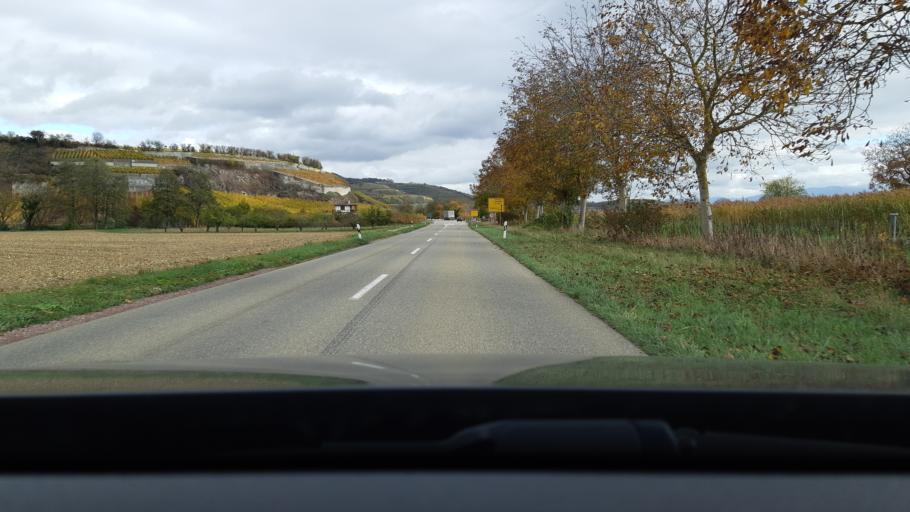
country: DE
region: Baden-Wuerttemberg
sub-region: Freiburg Region
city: Ihringen
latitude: 48.0371
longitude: 7.6207
